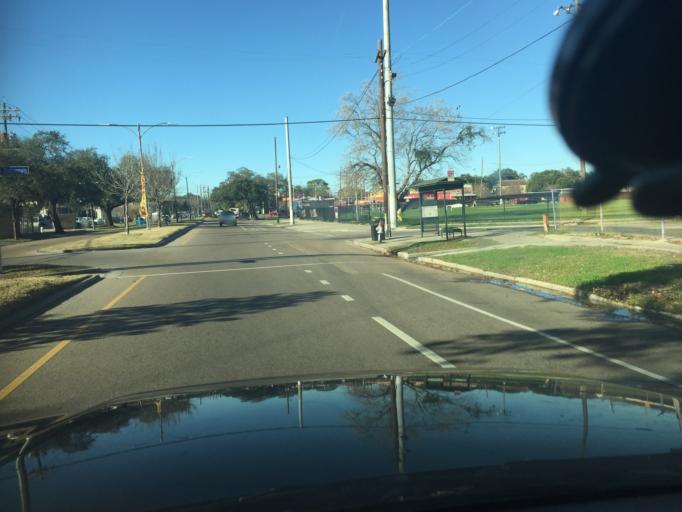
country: US
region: Louisiana
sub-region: Orleans Parish
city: New Orleans
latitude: 29.9816
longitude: -90.0707
